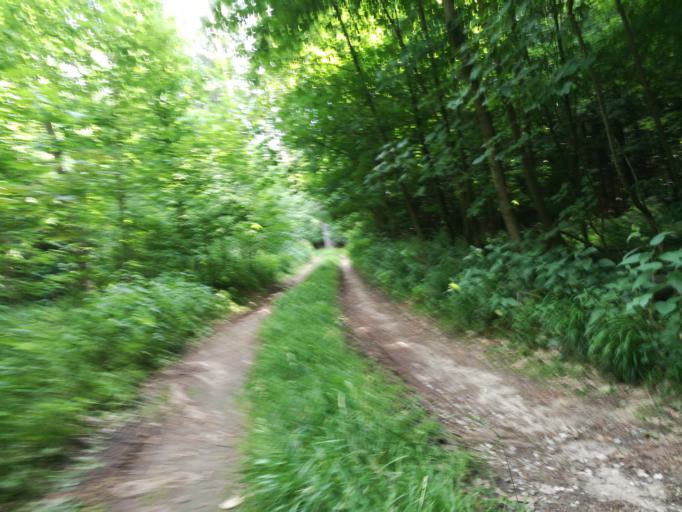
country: DE
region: Bavaria
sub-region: Regierungsbezirk Mittelfranken
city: Obermichelbach
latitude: 49.5063
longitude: 10.9194
